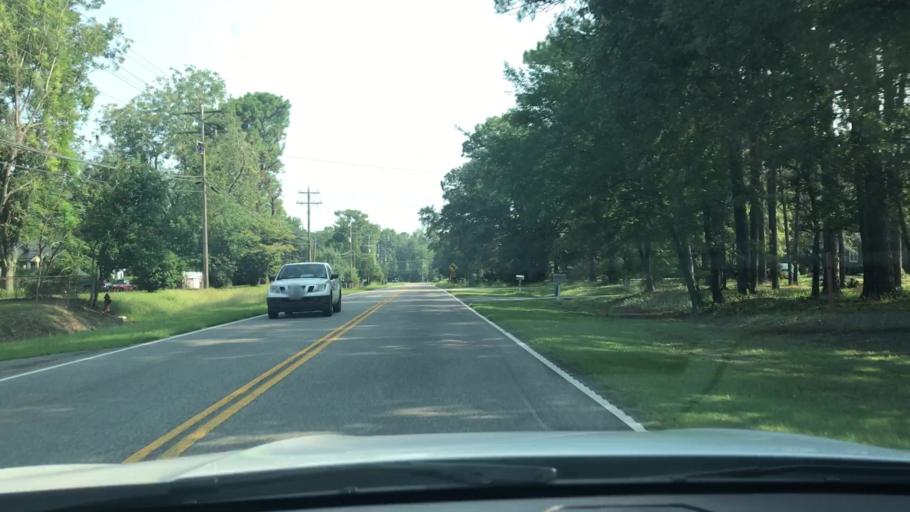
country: US
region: South Carolina
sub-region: Georgetown County
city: Georgetown
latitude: 33.4338
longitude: -79.2774
